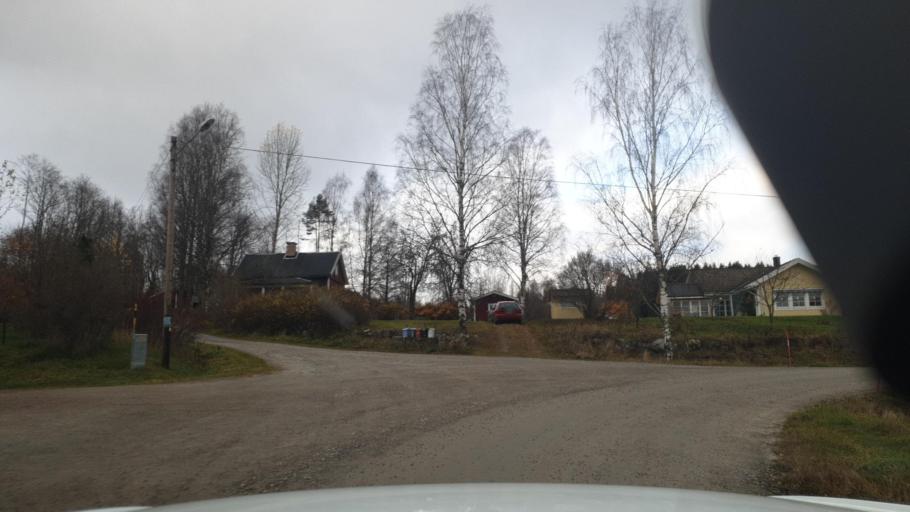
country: SE
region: Vaermland
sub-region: Arvika Kommun
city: Arvika
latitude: 59.6664
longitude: 12.7577
